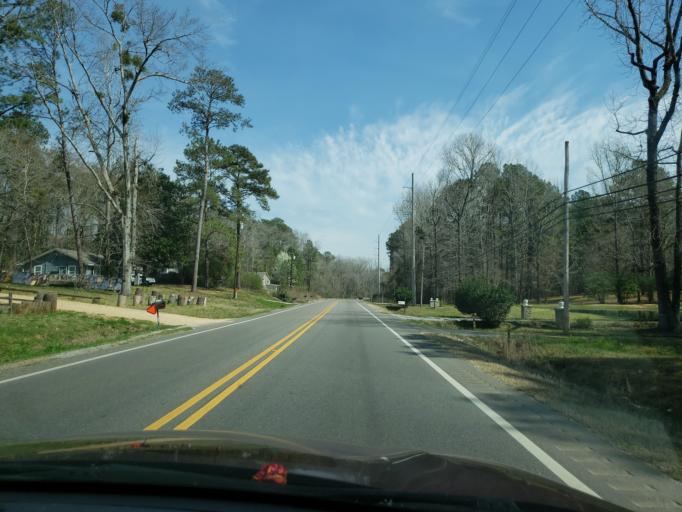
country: US
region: Alabama
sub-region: Elmore County
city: Wetumpka
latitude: 32.5525
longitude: -86.1727
